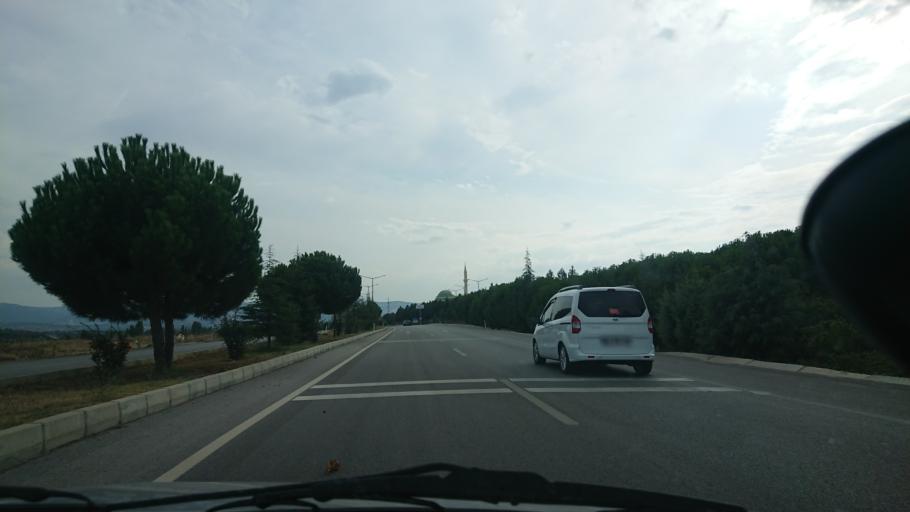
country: TR
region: Kuetahya
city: Gediz
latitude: 39.0077
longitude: 29.4068
